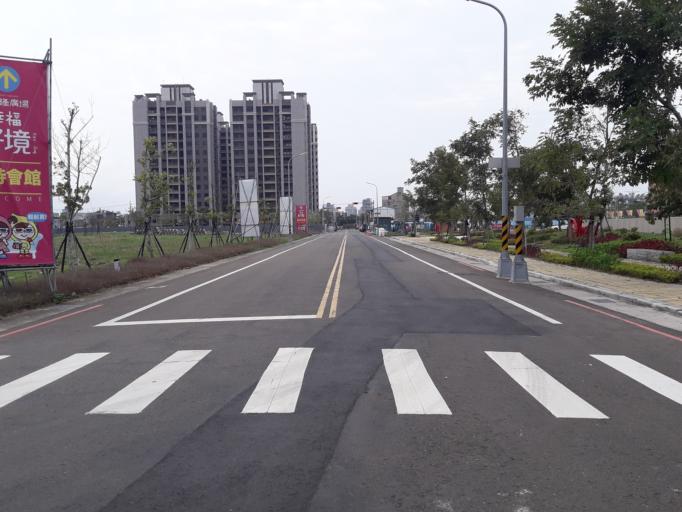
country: TW
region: Taiwan
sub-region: Hsinchu
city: Hsinchu
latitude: 24.6886
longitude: 120.8991
